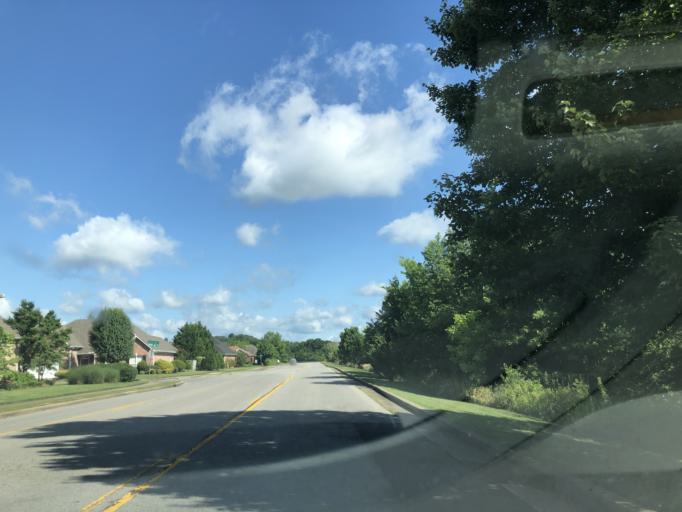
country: US
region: Tennessee
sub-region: Davidson County
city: Belle Meade
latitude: 36.0588
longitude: -86.9475
